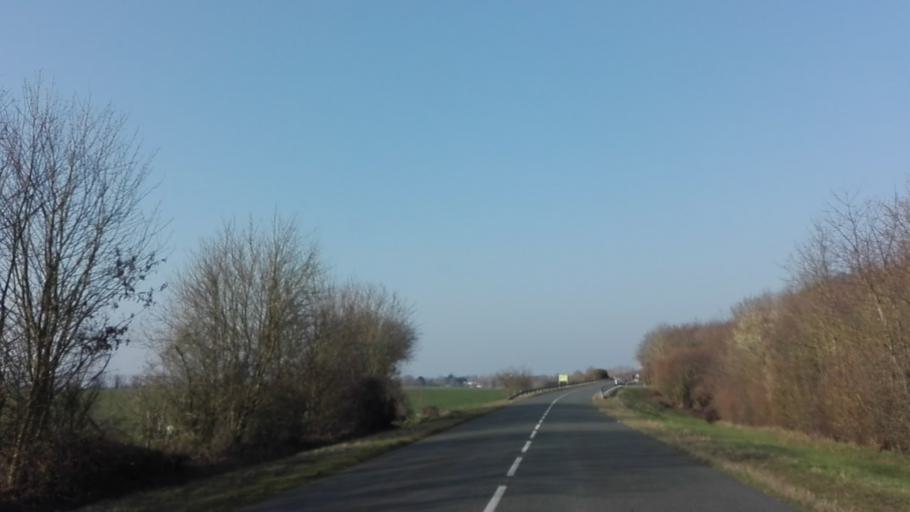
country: FR
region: Pays de la Loire
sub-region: Departement de la Vendee
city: Les Brouzils
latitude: 46.9047
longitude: -1.3183
